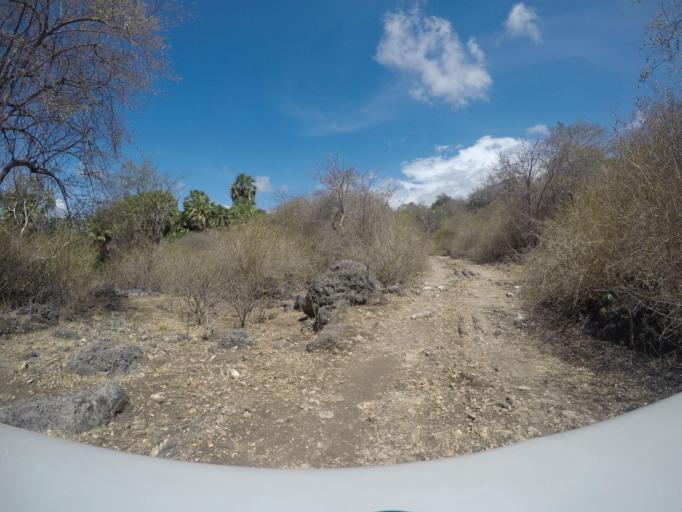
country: TL
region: Baucau
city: Baucau
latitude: -8.4417
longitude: 126.4406
